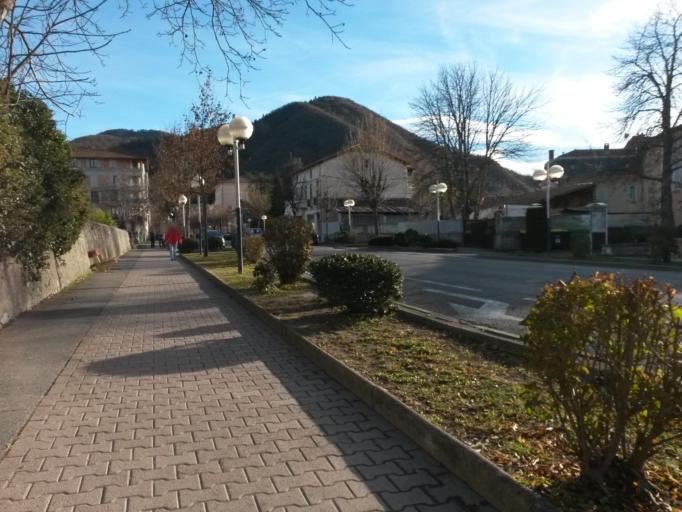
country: FR
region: Provence-Alpes-Cote d'Azur
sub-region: Departement des Alpes-de-Haute-Provence
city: Digne-les-Bains
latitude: 44.0964
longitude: 6.2346
